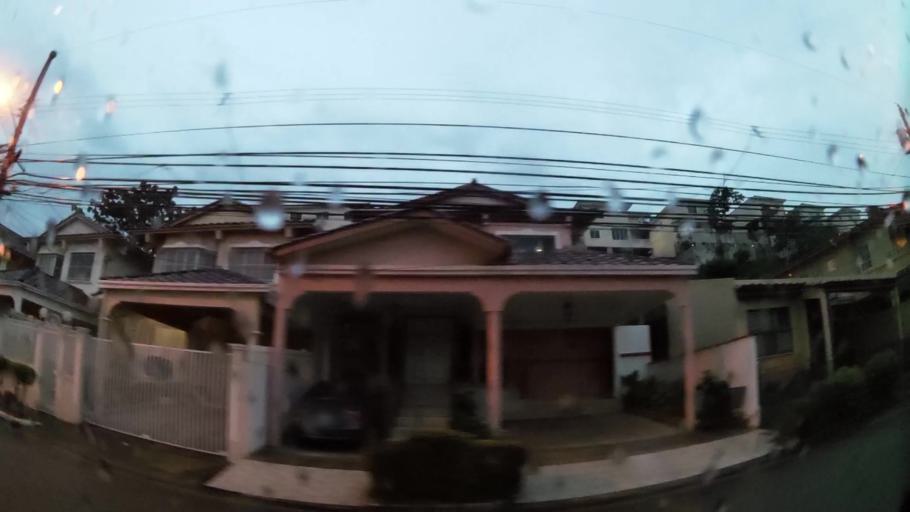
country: PA
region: Panama
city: Las Cumbres
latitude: 9.0439
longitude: -79.5222
